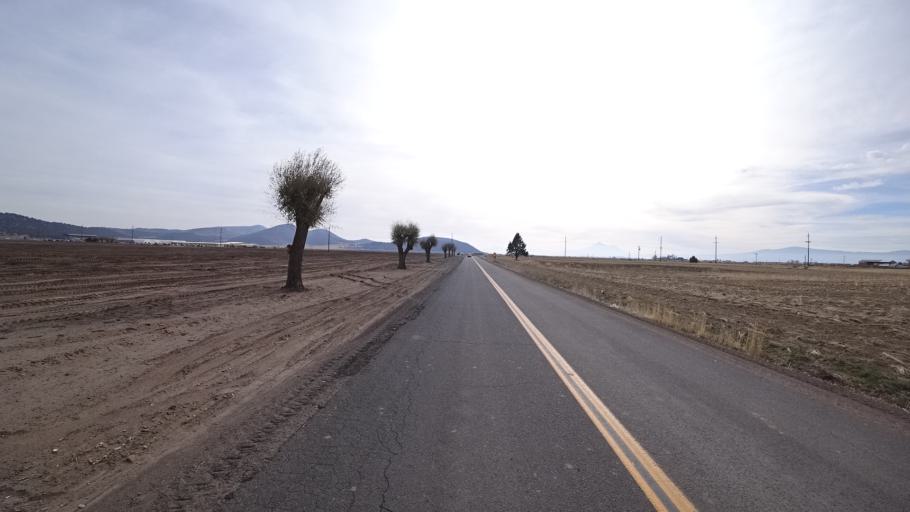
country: US
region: Oregon
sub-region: Klamath County
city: Klamath Falls
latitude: 41.9623
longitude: -121.9115
